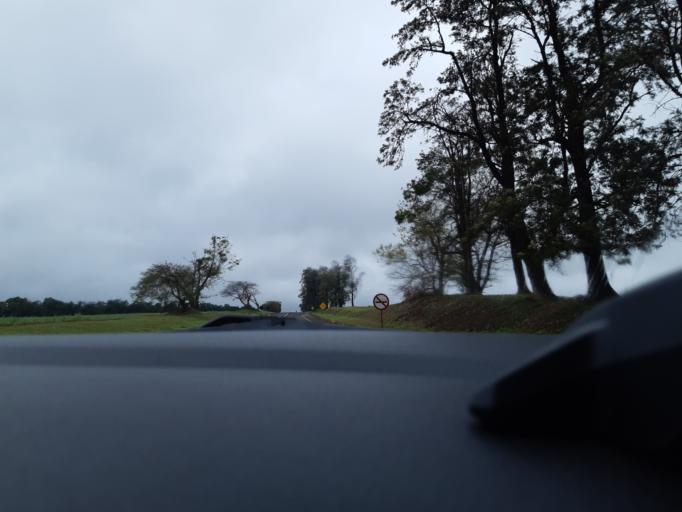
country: BR
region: Sao Paulo
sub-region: Ourinhos
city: Ourinhos
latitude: -23.0013
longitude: -49.9478
